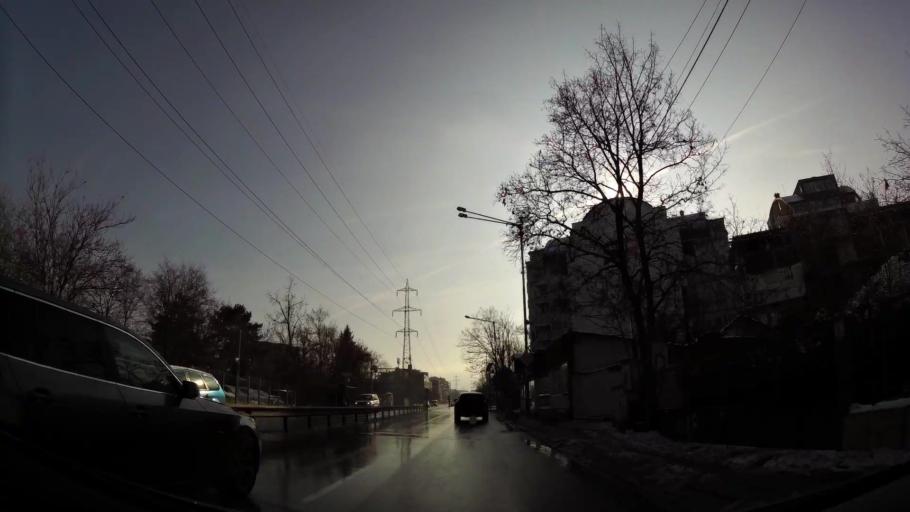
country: BG
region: Sofia-Capital
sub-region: Stolichna Obshtina
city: Sofia
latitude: 42.6559
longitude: 23.3362
